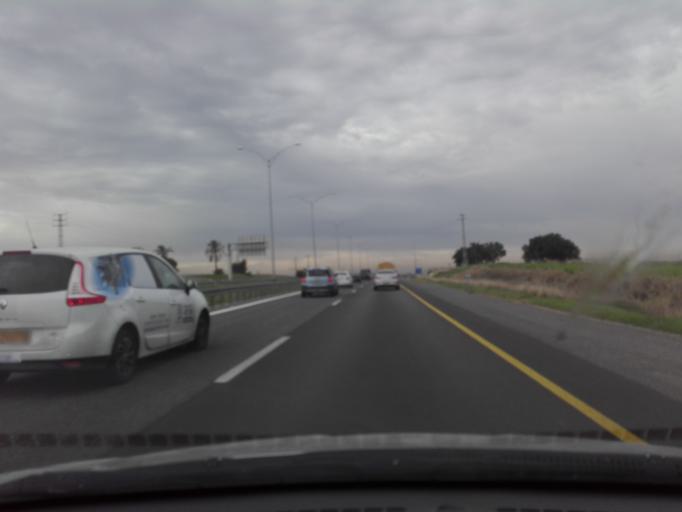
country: IL
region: Central District
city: Ramla
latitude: 31.8878
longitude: 34.8809
